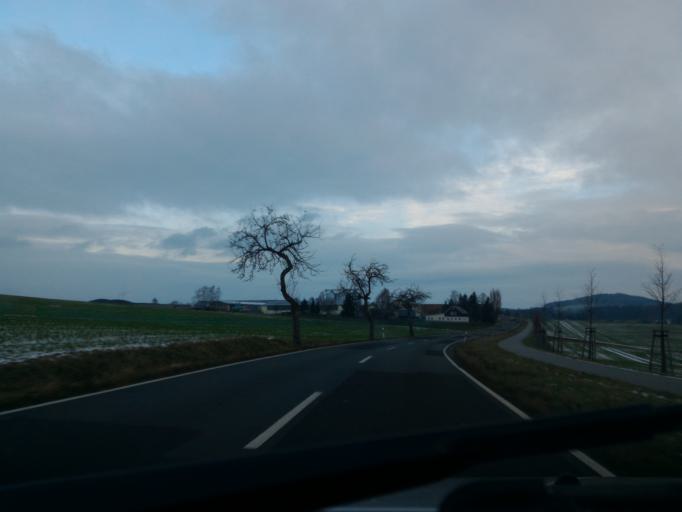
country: DE
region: Saxony
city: Leutersdorf
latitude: 50.9393
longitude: 14.6692
